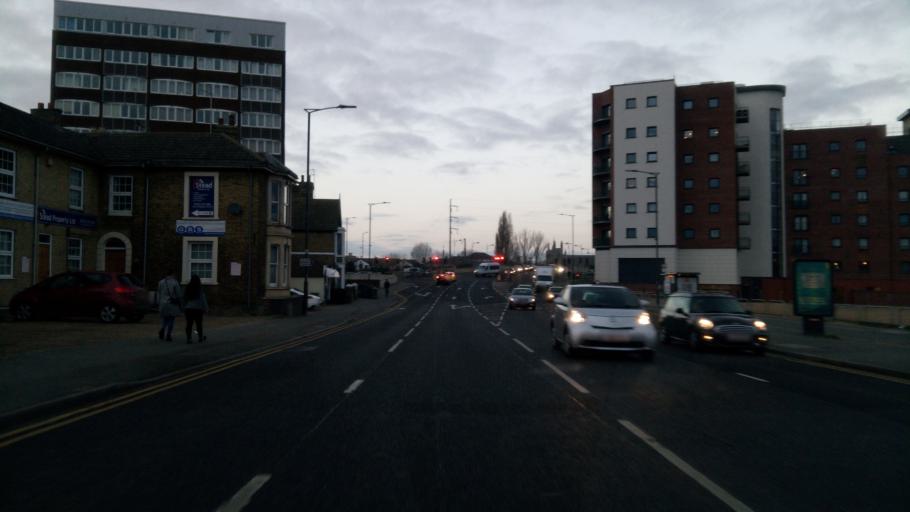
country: GB
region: England
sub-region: Peterborough
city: Peterborough
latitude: 52.5652
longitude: -0.2422
